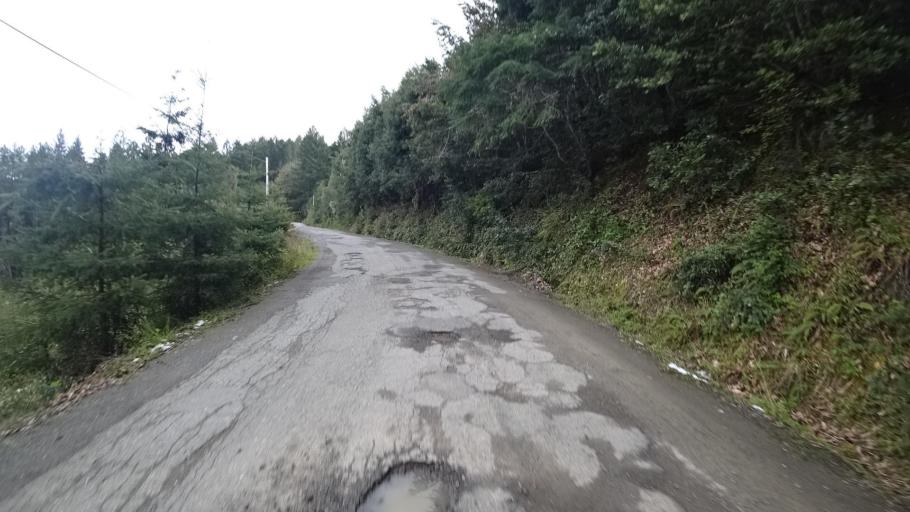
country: US
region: California
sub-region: Humboldt County
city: Blue Lake
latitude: 40.8712
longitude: -123.8964
